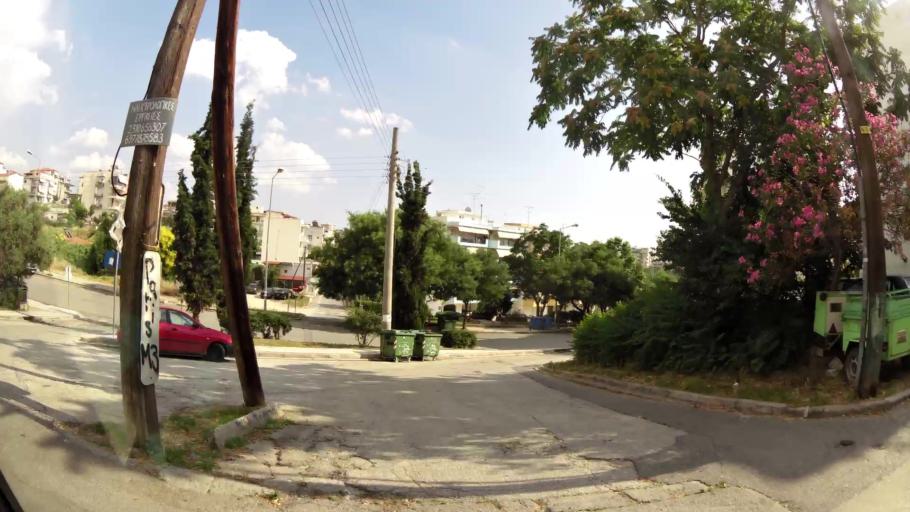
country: GR
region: Central Macedonia
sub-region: Nomos Thessalonikis
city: Polichni
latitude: 40.6611
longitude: 22.9515
